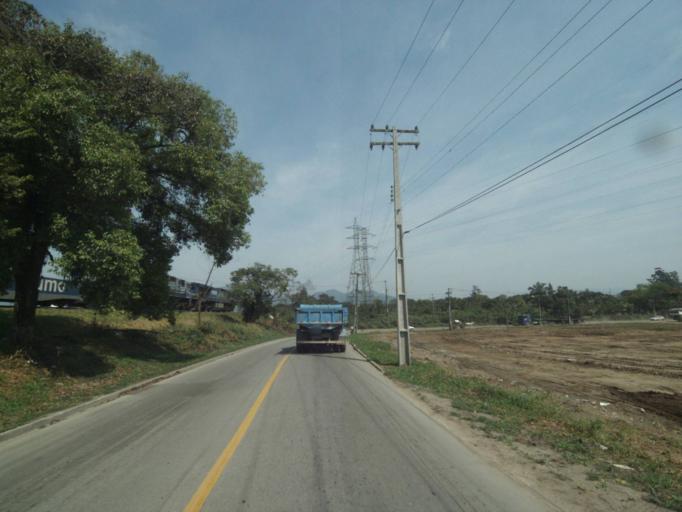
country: BR
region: Parana
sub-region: Paranagua
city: Paranagua
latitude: -25.5491
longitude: -48.5553
